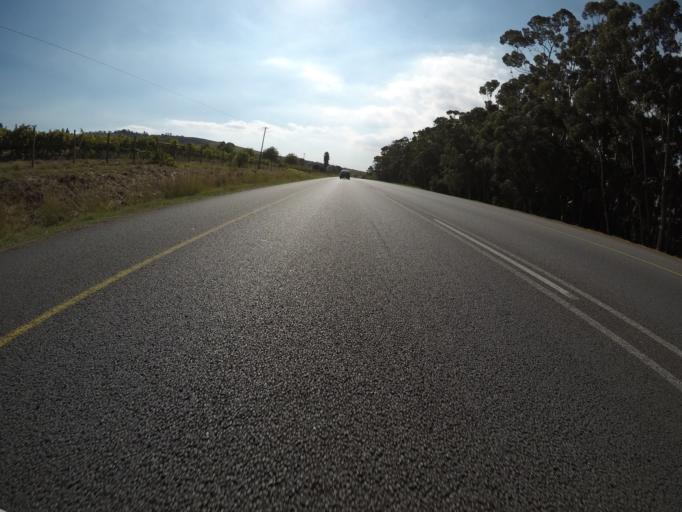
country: ZA
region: Western Cape
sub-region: Cape Winelands District Municipality
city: Stellenbosch
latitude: -33.8940
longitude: 18.8316
